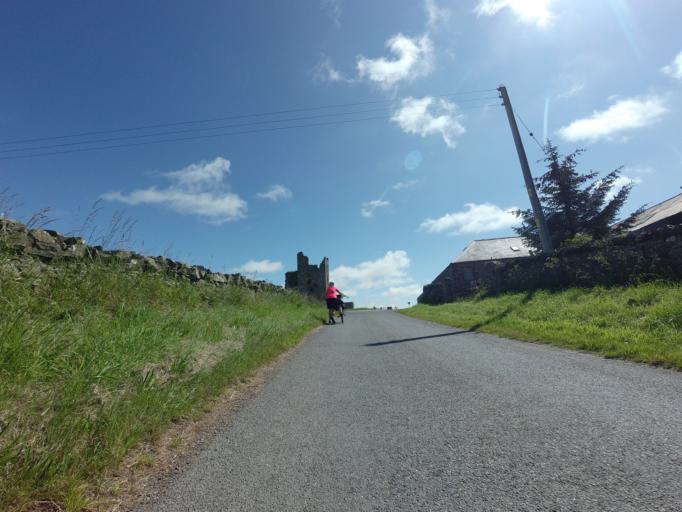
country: GB
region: Scotland
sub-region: Aberdeenshire
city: Banff
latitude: 57.6179
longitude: -2.5083
